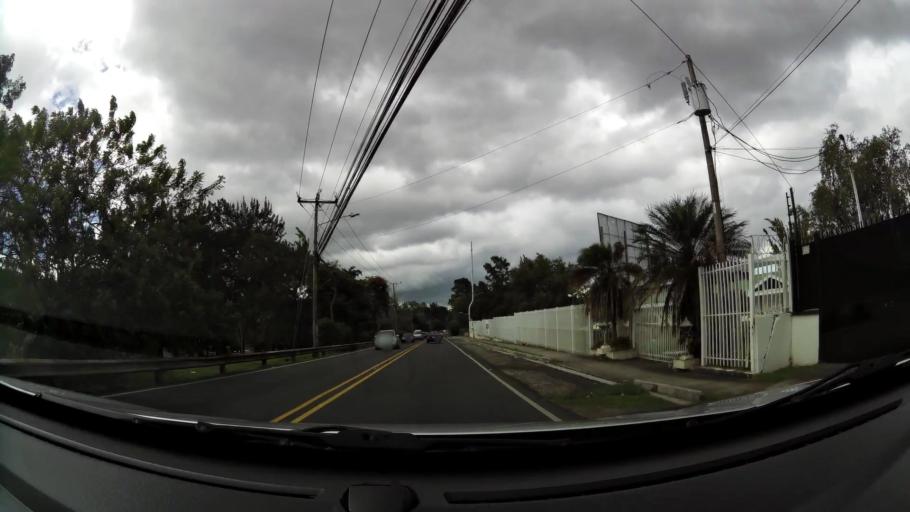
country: CR
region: San Jose
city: Curridabat
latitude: 9.9129
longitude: -84.0249
